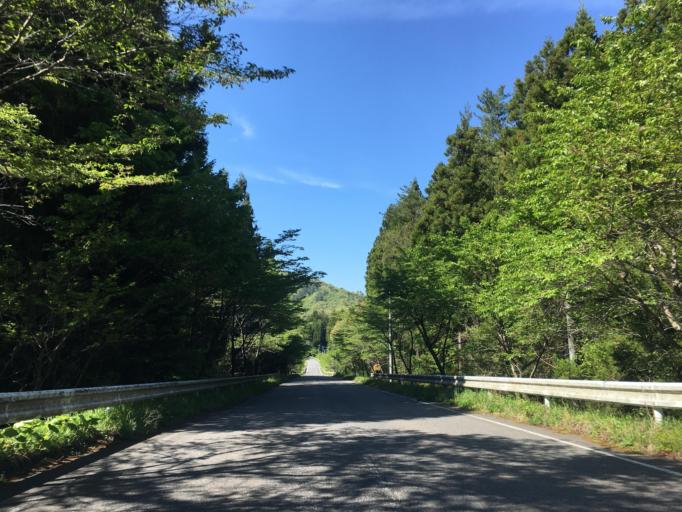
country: JP
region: Fukushima
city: Funehikimachi-funehiki
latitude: 37.3479
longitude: 140.6315
